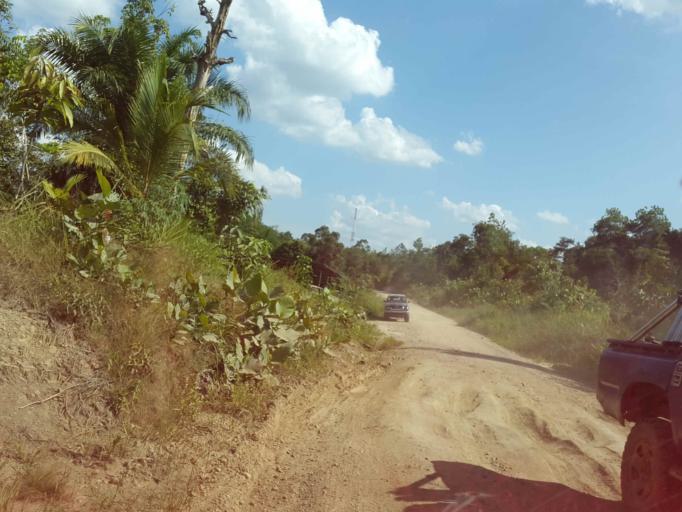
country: MY
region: Sarawak
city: Simanggang
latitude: 0.7121
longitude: 111.5372
